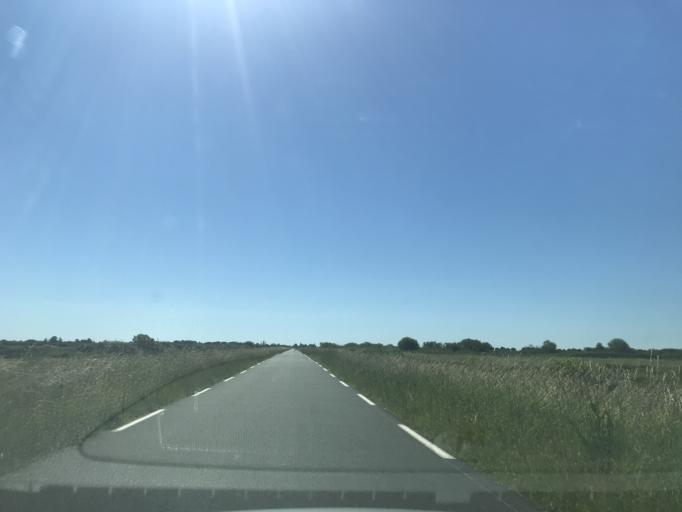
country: FR
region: Aquitaine
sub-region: Departement de la Gironde
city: Braud-et-Saint-Louis
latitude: 45.2879
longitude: -0.6674
